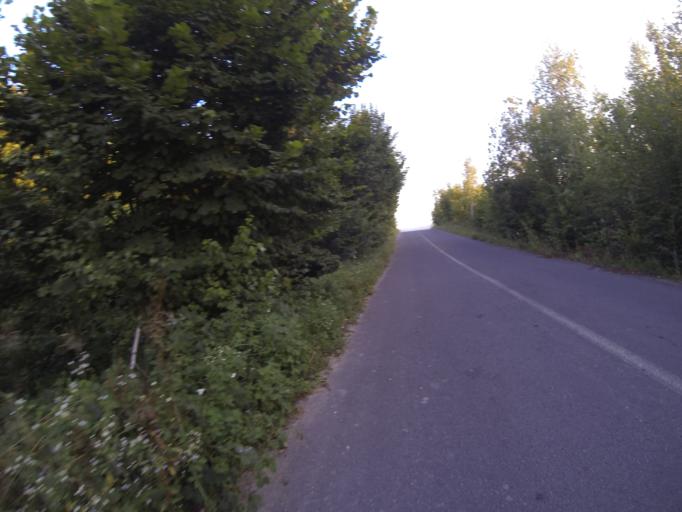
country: RO
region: Brasov
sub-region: Comuna Sinca Veche
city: Sinca Veche
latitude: 45.7516
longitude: 25.1654
